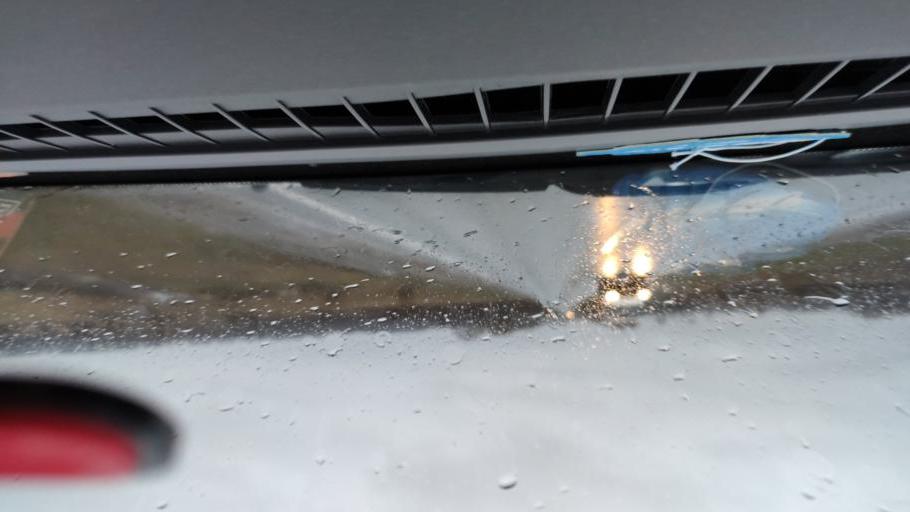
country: RU
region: Tatarstan
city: Mendeleyevsk
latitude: 55.9686
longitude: 52.3172
